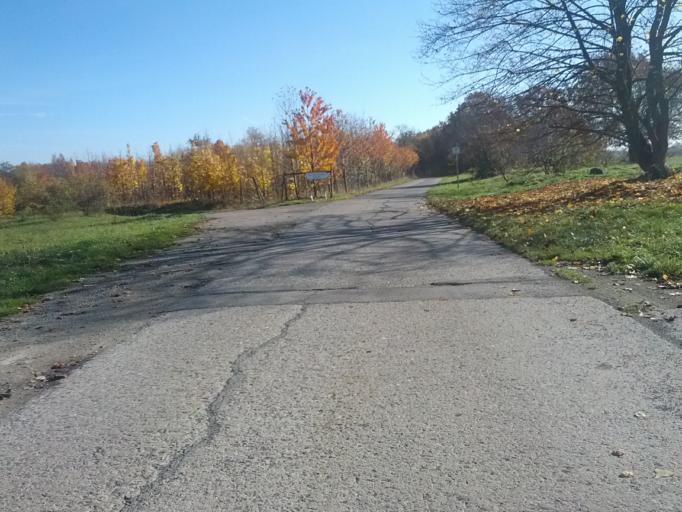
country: DE
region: Thuringia
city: Haina
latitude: 50.9942
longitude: 10.4852
